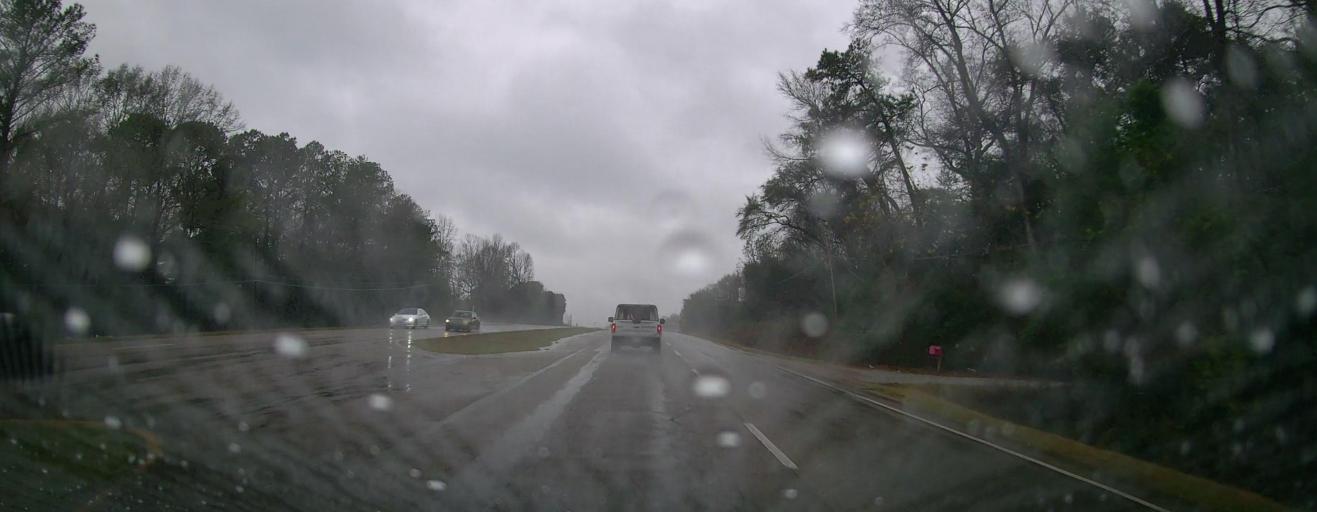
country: US
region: Alabama
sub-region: Autauga County
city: Prattville
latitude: 32.4293
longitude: -86.4145
